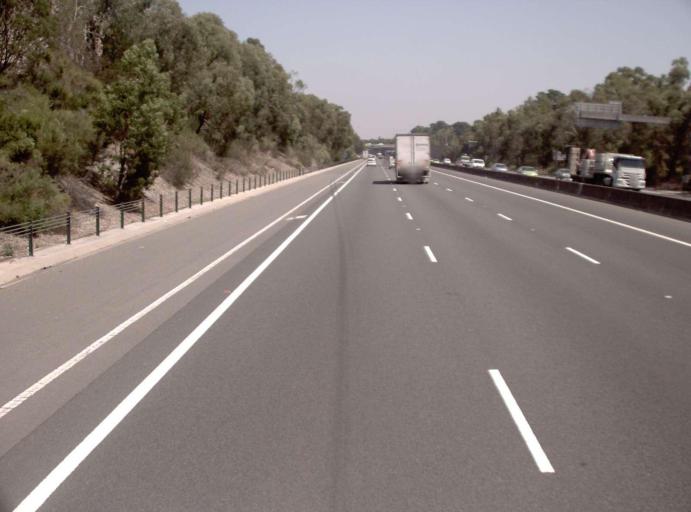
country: AU
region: Victoria
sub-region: Whitehorse
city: Blackburn North
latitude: -37.8029
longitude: 145.1663
